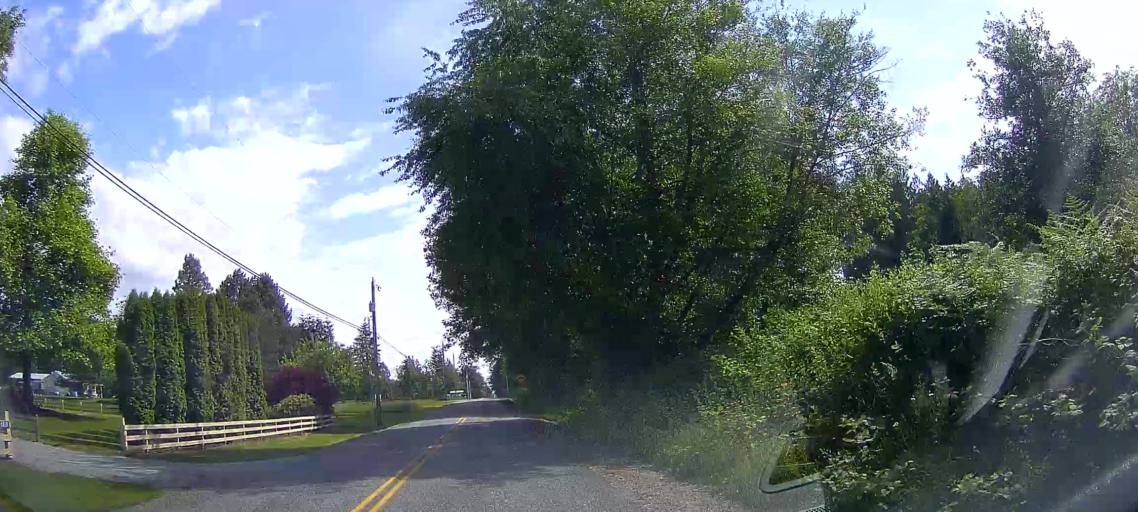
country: US
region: Washington
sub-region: Skagit County
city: Burlington
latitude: 48.5617
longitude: -122.3618
